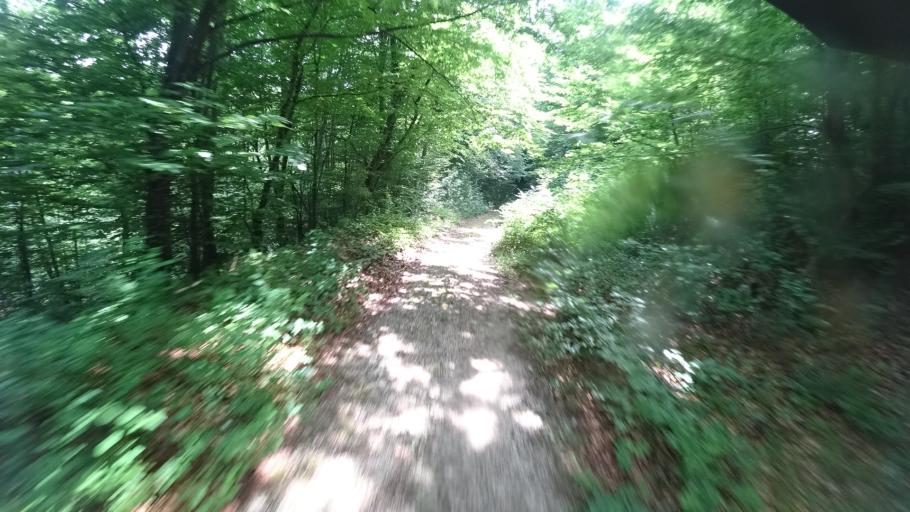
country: HR
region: Licko-Senjska
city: Jezerce
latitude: 44.8802
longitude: 15.7005
